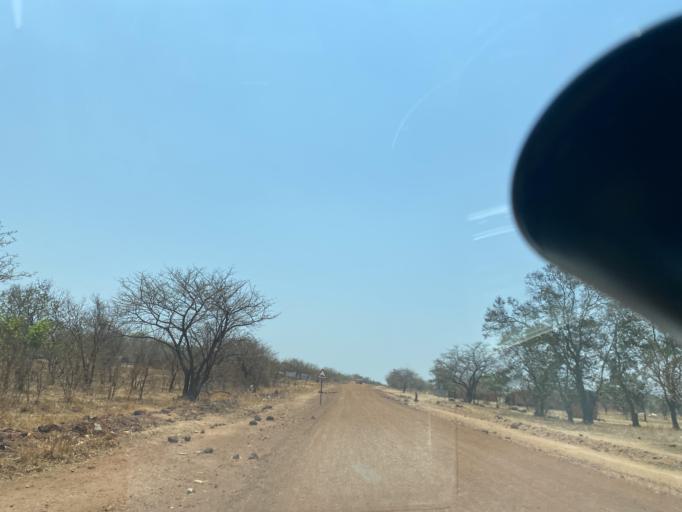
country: ZM
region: Lusaka
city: Lusaka
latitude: -15.4517
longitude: 27.9501
